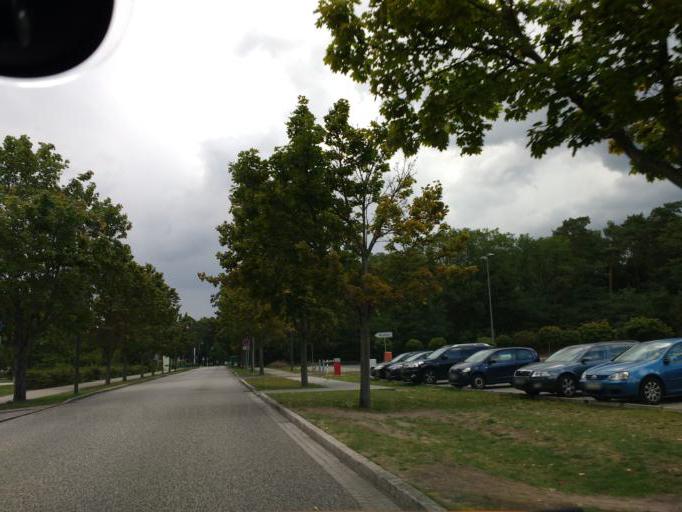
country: DE
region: Brandenburg
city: Bad Saarow
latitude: 52.2847
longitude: 14.0648
